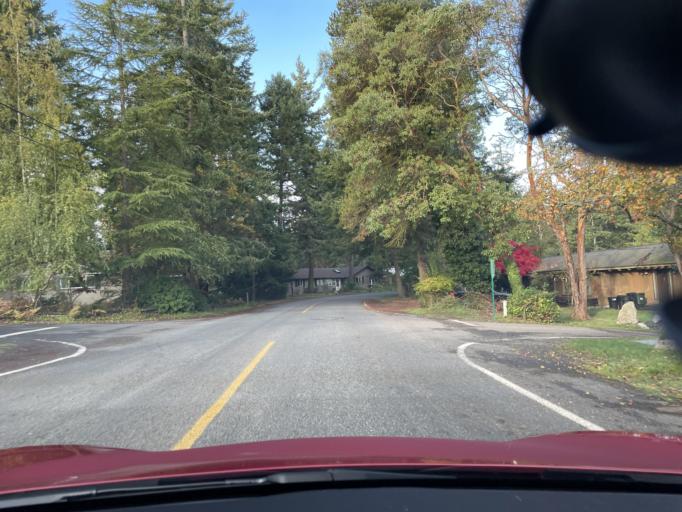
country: US
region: Washington
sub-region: San Juan County
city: Friday Harbor
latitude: 48.5345
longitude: -123.0292
